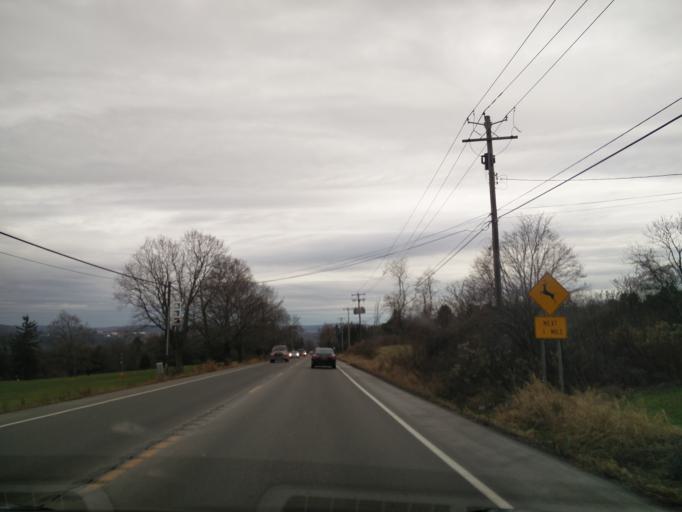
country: US
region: New York
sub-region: Tompkins County
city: Northwest Ithaca
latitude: 42.4649
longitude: -76.5368
